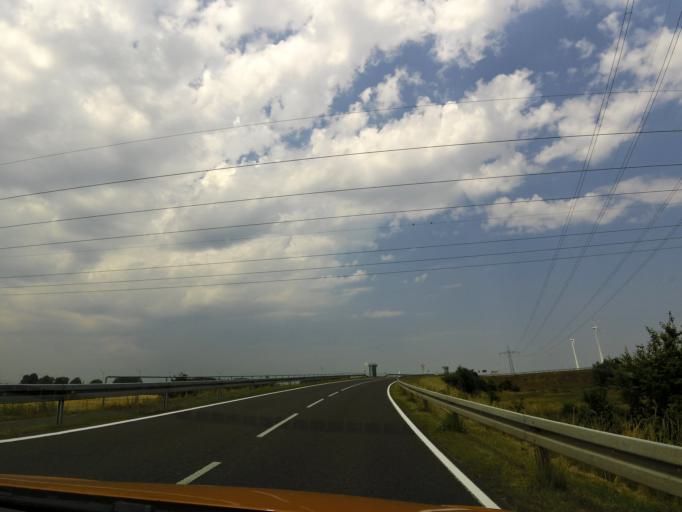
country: DE
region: Brandenburg
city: Wustermark
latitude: 52.5580
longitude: 12.9273
